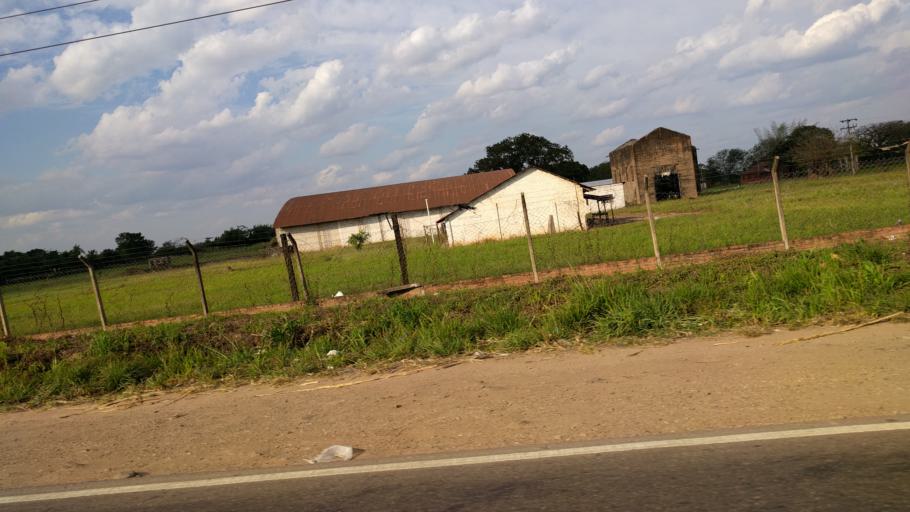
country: BO
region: Santa Cruz
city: Warnes
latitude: -17.5460
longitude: -63.1603
